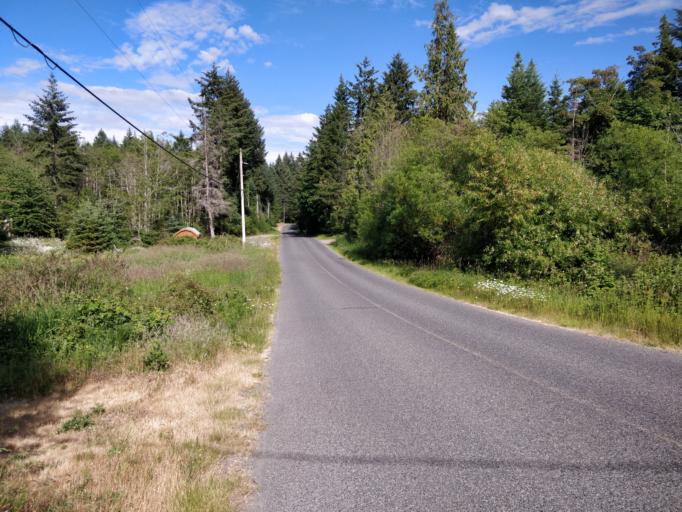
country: CA
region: British Columbia
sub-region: Cowichan Valley Regional District
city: Ladysmith
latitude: 49.0791
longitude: -123.7996
